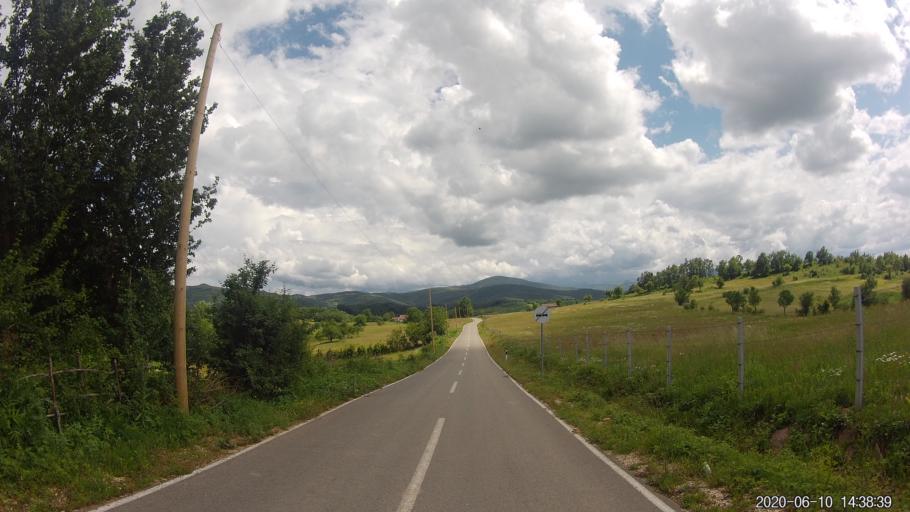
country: XK
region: Prizren
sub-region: Komuna e Therandes
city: Budakovo
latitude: 42.4037
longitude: 20.9420
